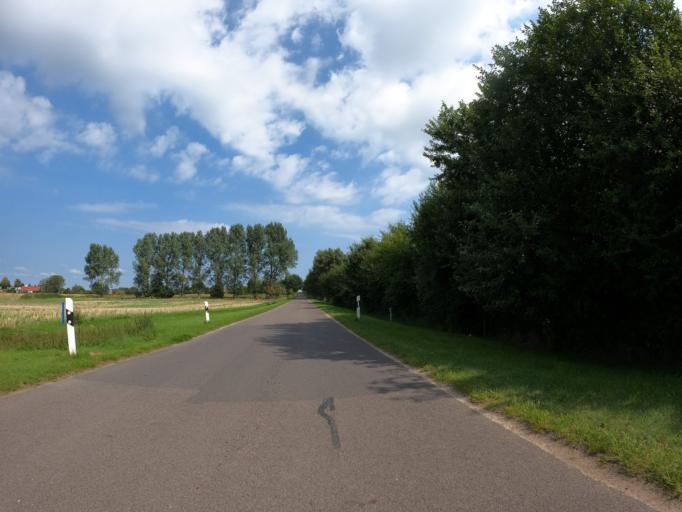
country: DE
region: Mecklenburg-Vorpommern
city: Malchow
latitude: 53.4573
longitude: 12.4775
